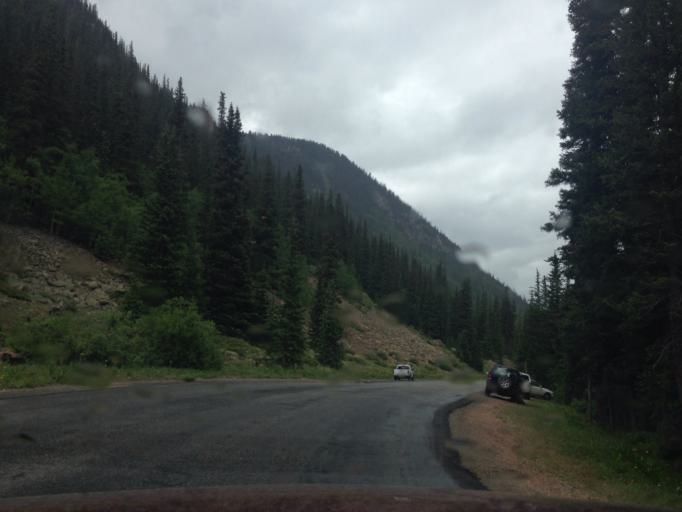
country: US
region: Colorado
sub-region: Clear Creek County
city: Georgetown
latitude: 39.6293
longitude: -105.7120
